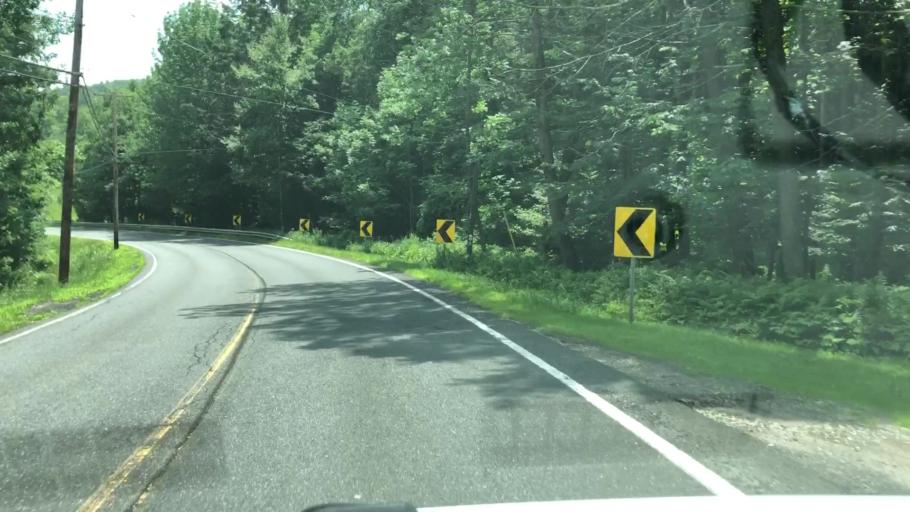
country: US
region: Massachusetts
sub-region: Hampshire County
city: Williamsburg
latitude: 42.4185
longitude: -72.7761
